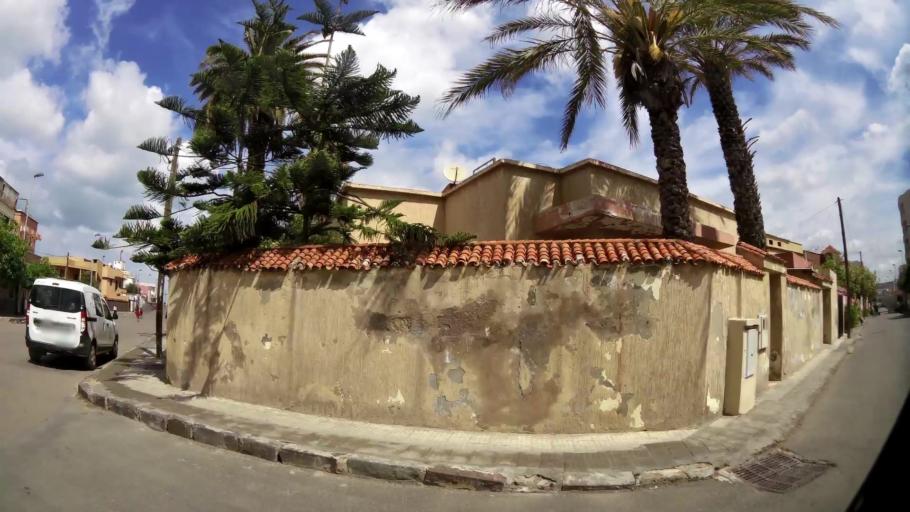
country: MA
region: Grand Casablanca
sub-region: Mediouna
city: Tit Mellil
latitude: 33.6178
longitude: -7.5371
